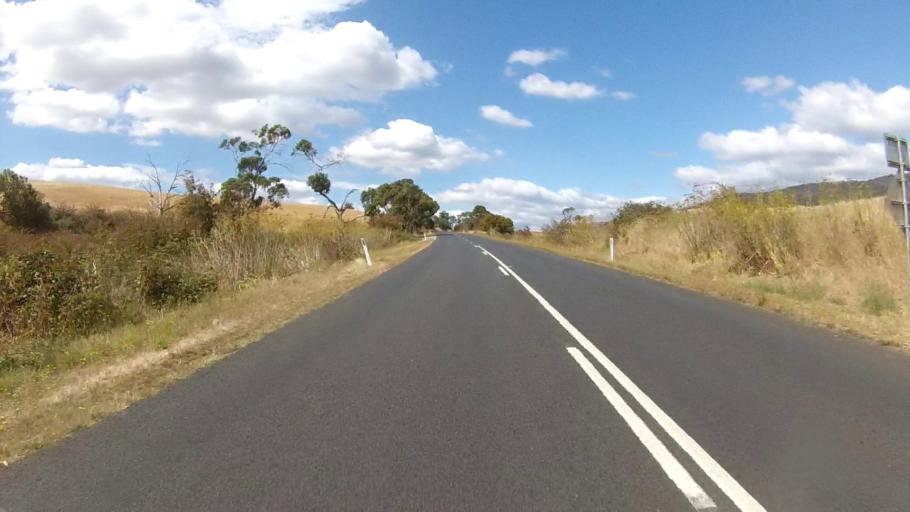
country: AU
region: Tasmania
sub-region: Derwent Valley
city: New Norfolk
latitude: -42.7337
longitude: 146.9264
